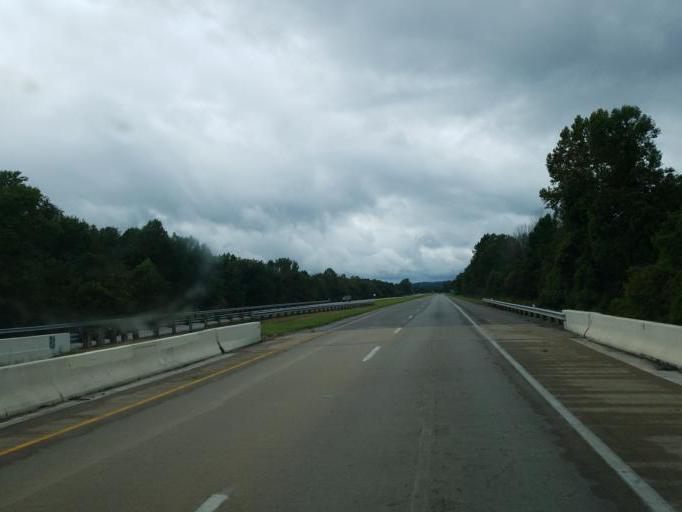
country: US
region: Ohio
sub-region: Scioto County
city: Wheelersburg
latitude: 38.7103
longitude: -82.8607
